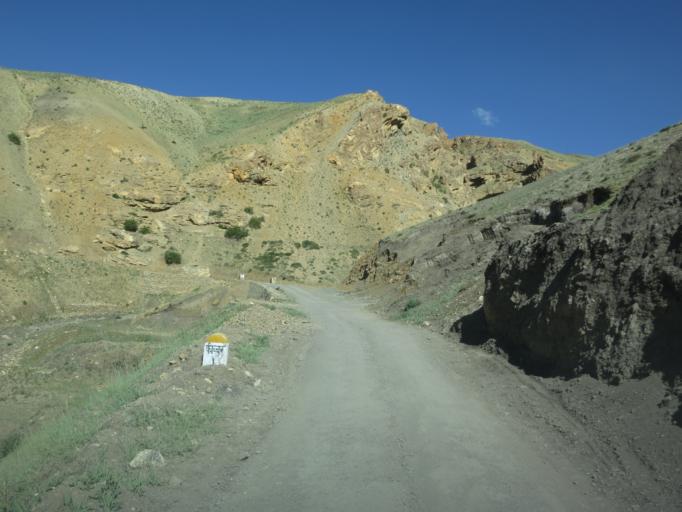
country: IN
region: Himachal Pradesh
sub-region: Kulu
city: Manali
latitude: 32.3248
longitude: 78.0084
